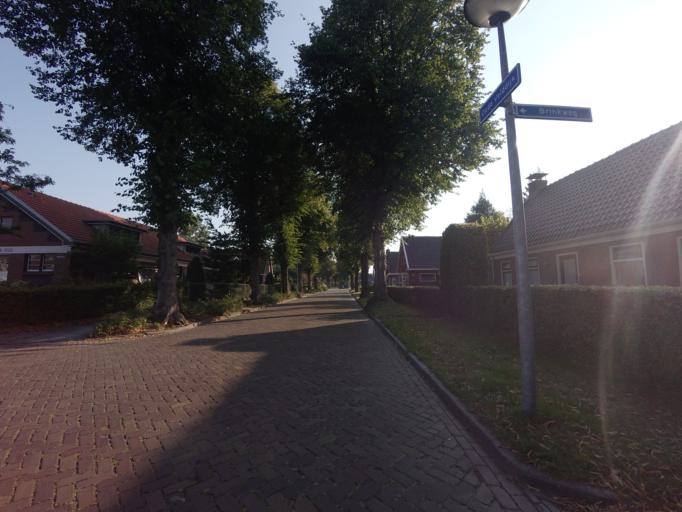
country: NL
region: Groningen
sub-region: Gemeente Groningen
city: Groningen
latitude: 53.1469
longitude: 6.4893
